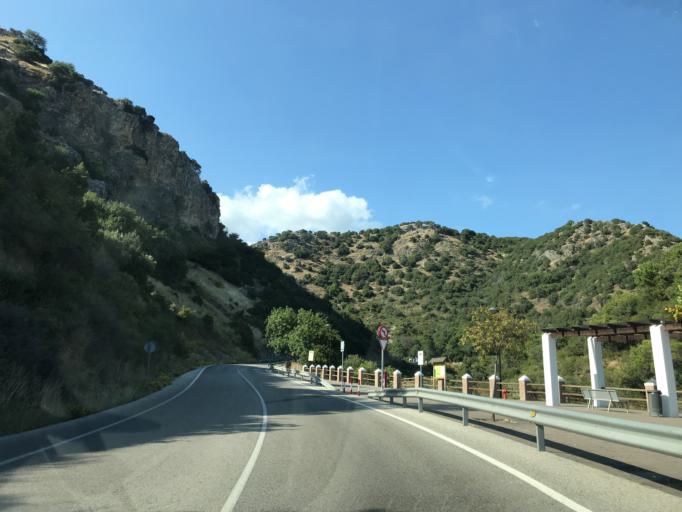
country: ES
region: Andalusia
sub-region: Provincia de Malaga
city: Benahavis
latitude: 36.5109
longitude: -5.0356
